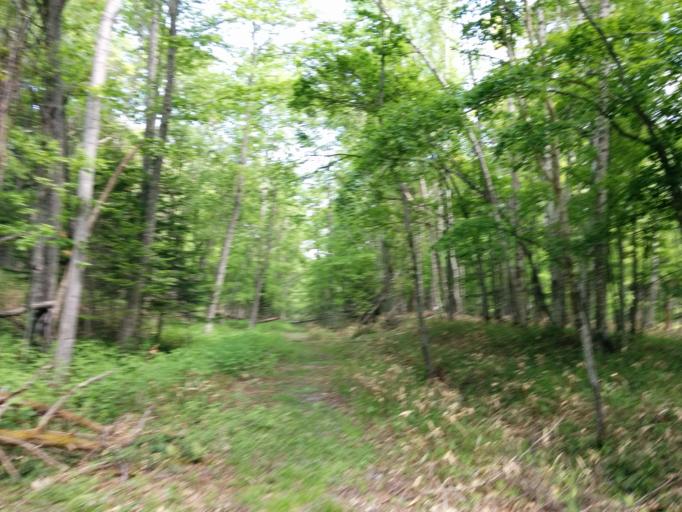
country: JP
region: Hokkaido
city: Otofuke
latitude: 43.3991
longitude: 143.1830
